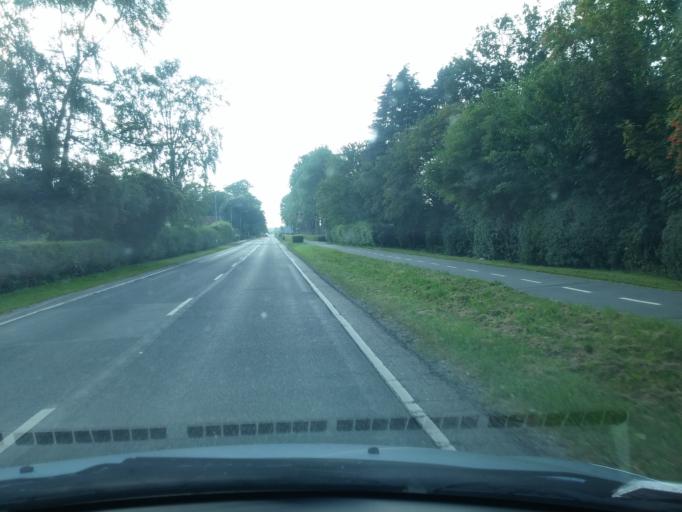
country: DK
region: South Denmark
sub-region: Odense Kommune
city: Bellinge
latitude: 55.3415
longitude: 10.2952
